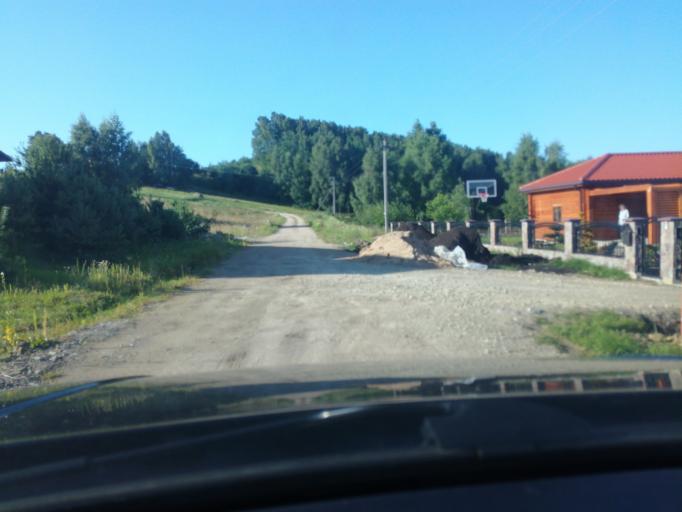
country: LT
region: Alytaus apskritis
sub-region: Alytus
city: Alytus
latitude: 54.4029
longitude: 23.9961
